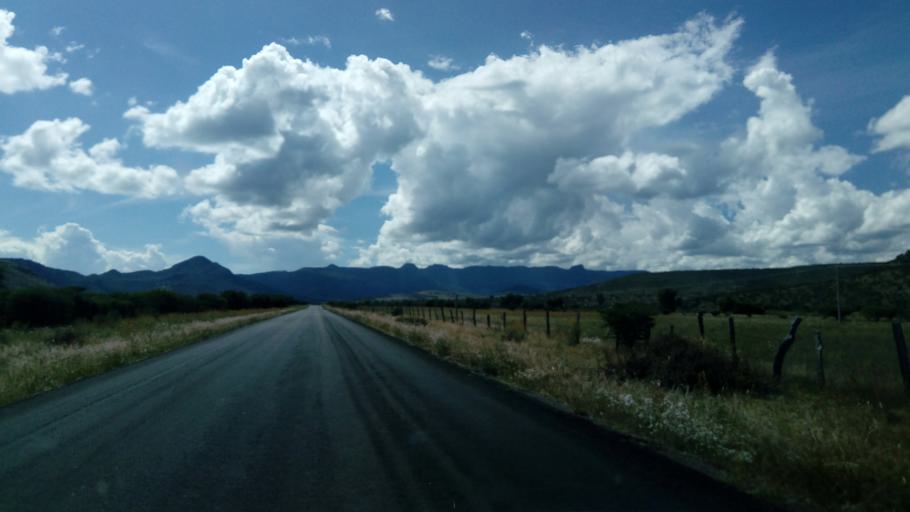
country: MX
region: Durango
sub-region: Durango
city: Jose Refugio Salcido
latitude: 23.8101
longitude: -104.4838
